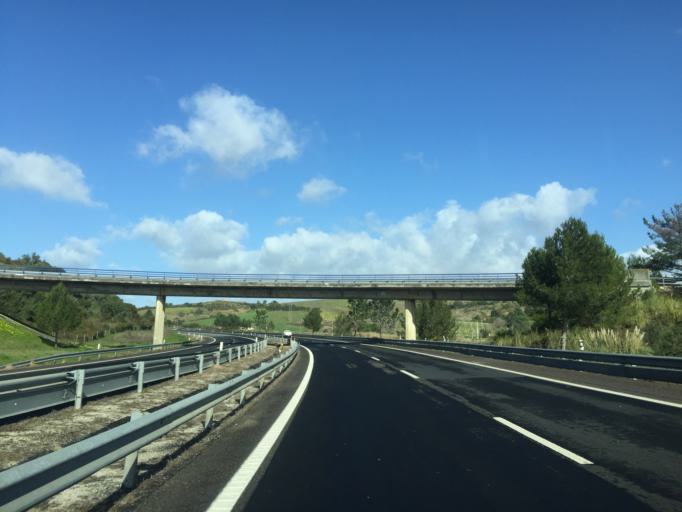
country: PT
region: Lisbon
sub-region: Torres Vedras
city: Torres Vedras
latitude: 39.0869
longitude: -9.2310
